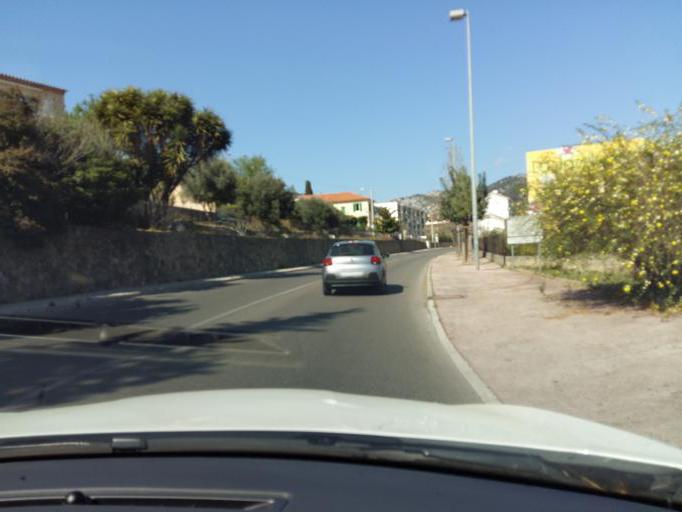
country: FR
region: Provence-Alpes-Cote d'Azur
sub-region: Departement du Var
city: Ollioules
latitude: 43.1305
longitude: 5.8442
